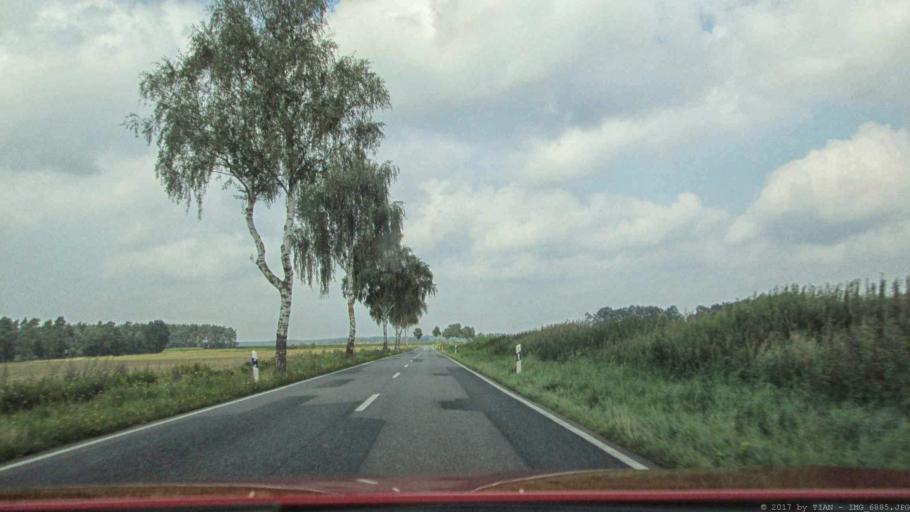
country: DE
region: Lower Saxony
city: Altenmedingen
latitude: 53.1163
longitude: 10.5986
